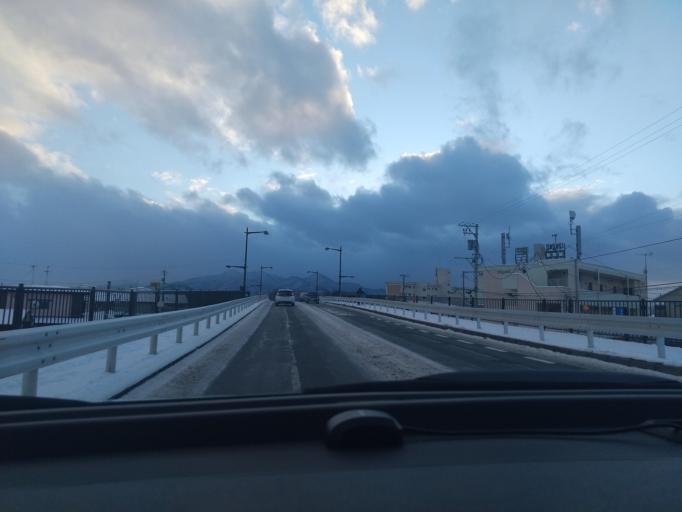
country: JP
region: Iwate
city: Morioka-shi
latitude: 39.7108
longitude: 141.1179
